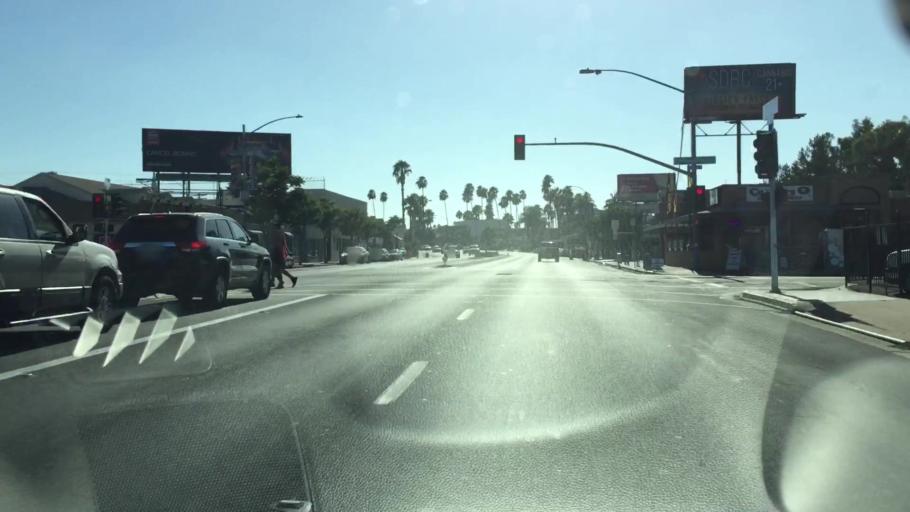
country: US
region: California
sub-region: San Diego County
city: La Mesa
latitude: 32.7671
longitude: -117.0571
